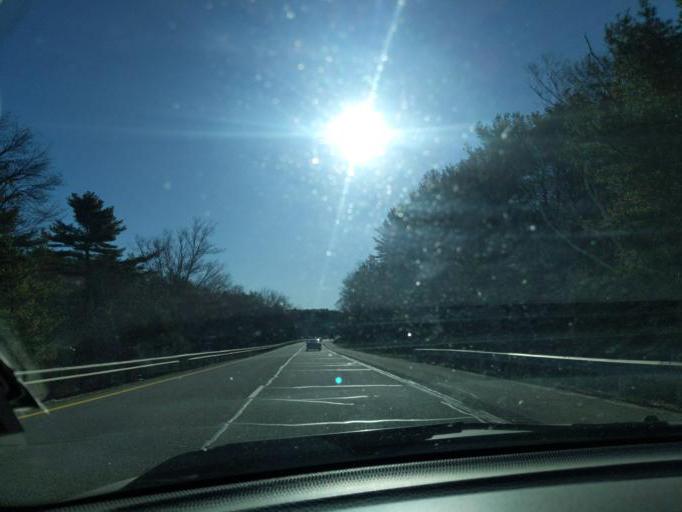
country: US
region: Massachusetts
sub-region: Essex County
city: Essex
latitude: 42.5912
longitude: -70.7811
